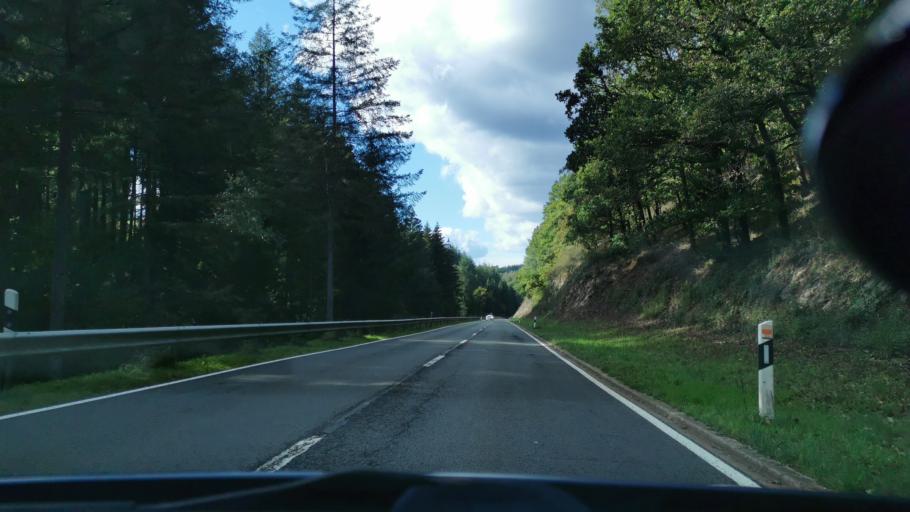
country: DE
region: Rheinland-Pfalz
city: Hupperath
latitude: 49.9991
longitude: 6.8164
